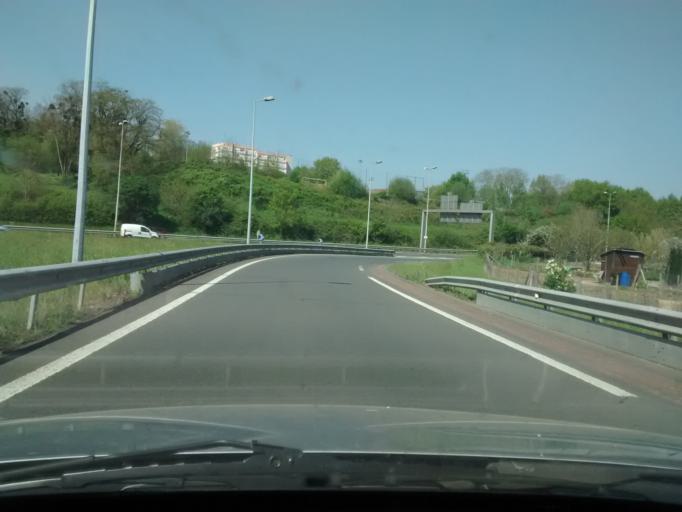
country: FR
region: Pays de la Loire
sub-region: Departement de la Sarthe
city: La Chapelle-Saint-Aubin
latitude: 48.0155
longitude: 0.1715
